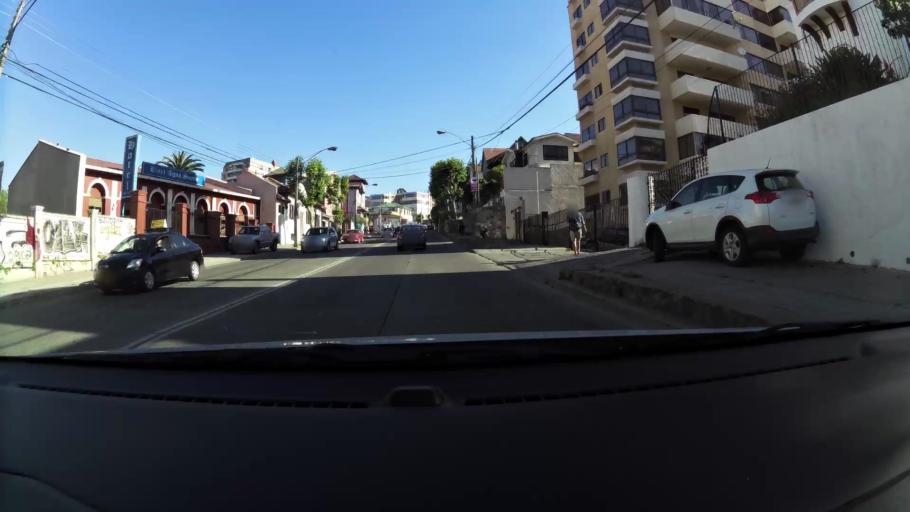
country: CL
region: Valparaiso
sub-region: Provincia de Valparaiso
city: Vina del Mar
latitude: -33.0265
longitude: -71.5629
